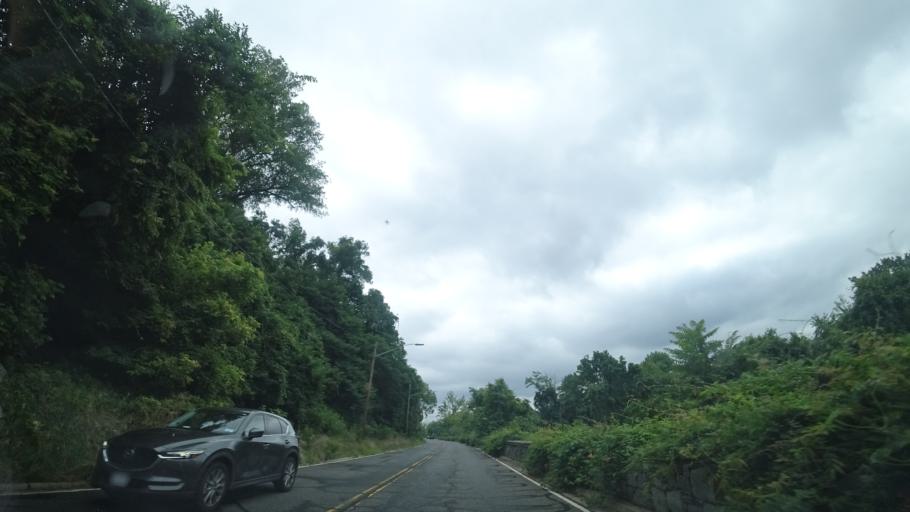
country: US
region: Virginia
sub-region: Arlington County
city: Arlington
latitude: 38.9093
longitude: -77.0906
